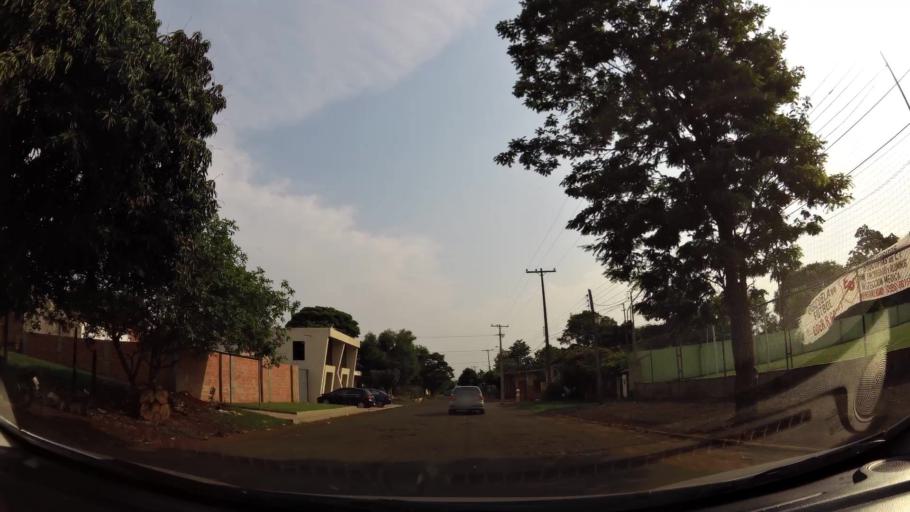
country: PY
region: Alto Parana
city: Ciudad del Este
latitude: -25.4867
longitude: -54.6554
